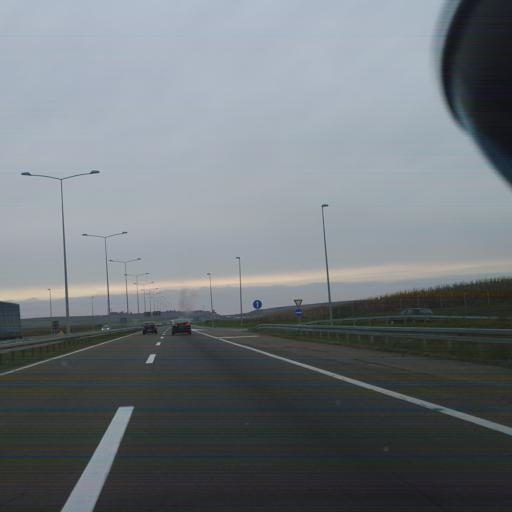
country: RS
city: Beska
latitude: 45.1367
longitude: 20.0873
